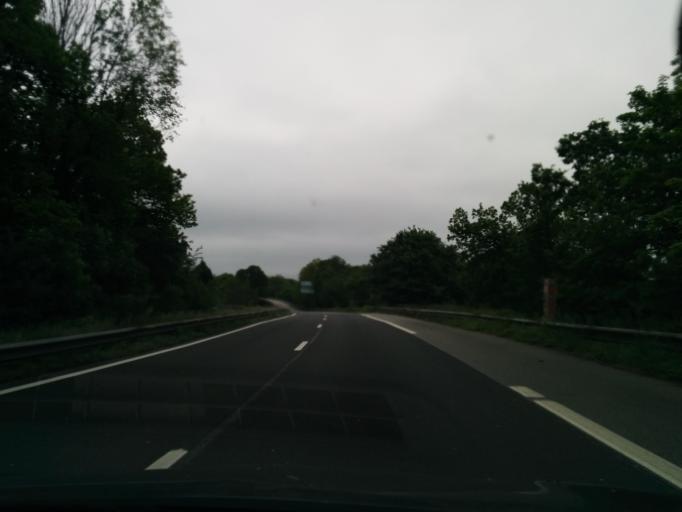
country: FR
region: Ile-de-France
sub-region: Departement des Yvelines
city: Rocquencourt
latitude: 48.8420
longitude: 2.0937
